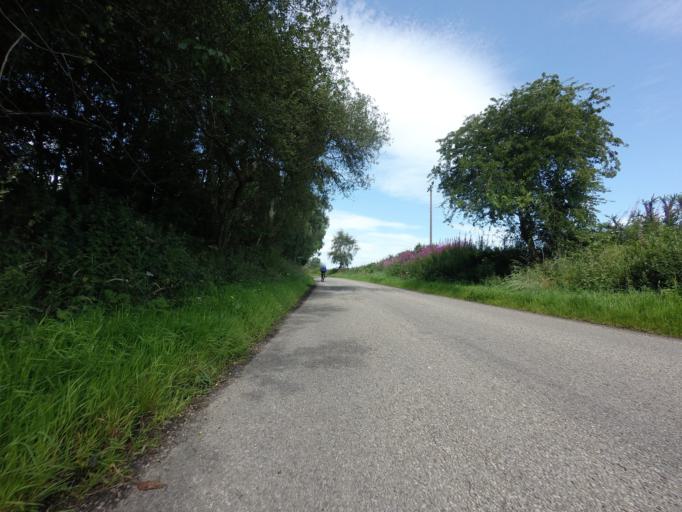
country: GB
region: Scotland
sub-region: Highland
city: Inverness
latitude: 57.5174
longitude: -4.2903
